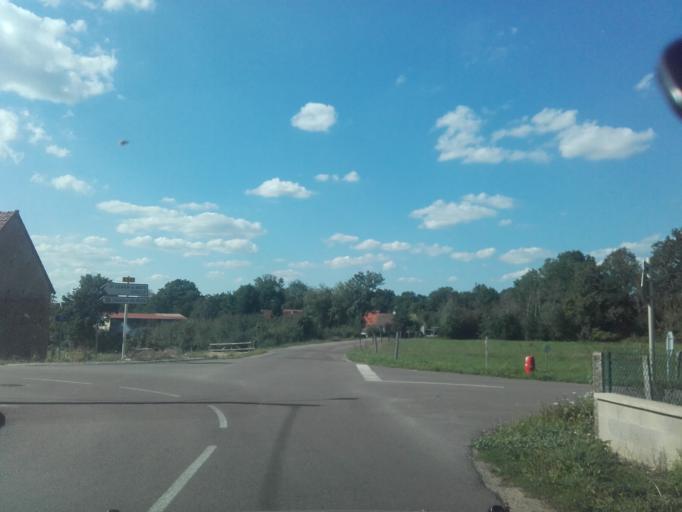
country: FR
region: Bourgogne
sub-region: Departement de Saone-et-Loire
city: Epinac
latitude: 46.9950
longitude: 4.5056
